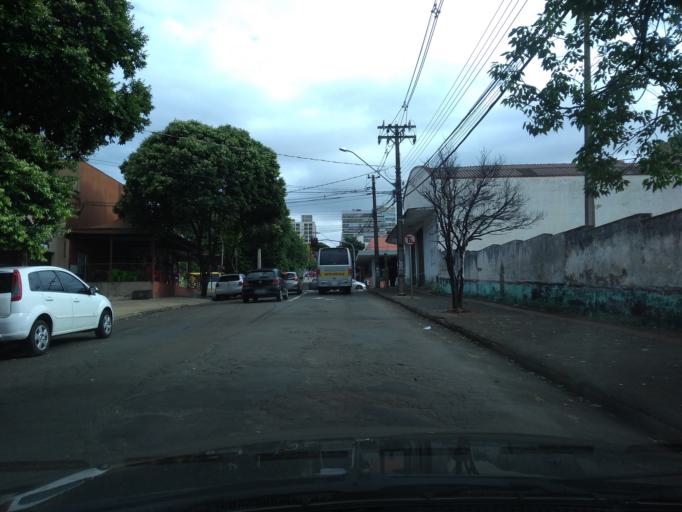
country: BR
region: Parana
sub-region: Londrina
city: Londrina
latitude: -23.3072
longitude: -51.1602
